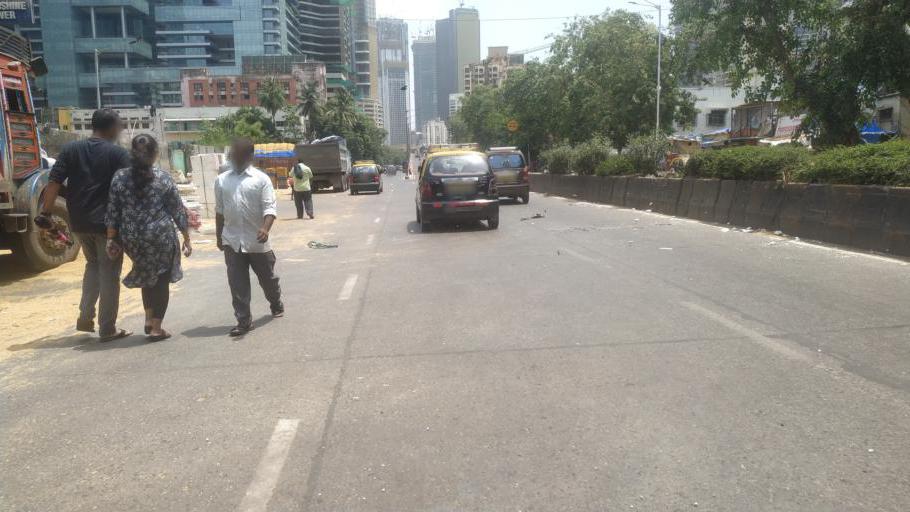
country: IN
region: Maharashtra
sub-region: Mumbai Suburban
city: Mumbai
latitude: 19.0125
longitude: 72.8365
